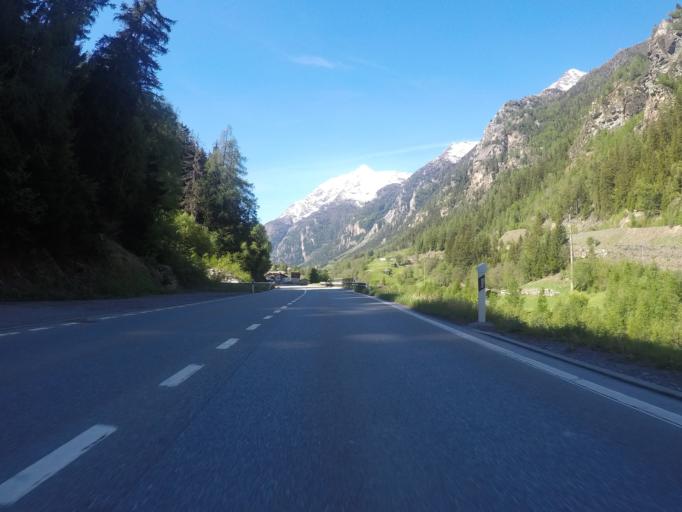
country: CH
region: Valais
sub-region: Visp District
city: Sankt Niklaus
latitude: 46.1913
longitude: 7.8139
